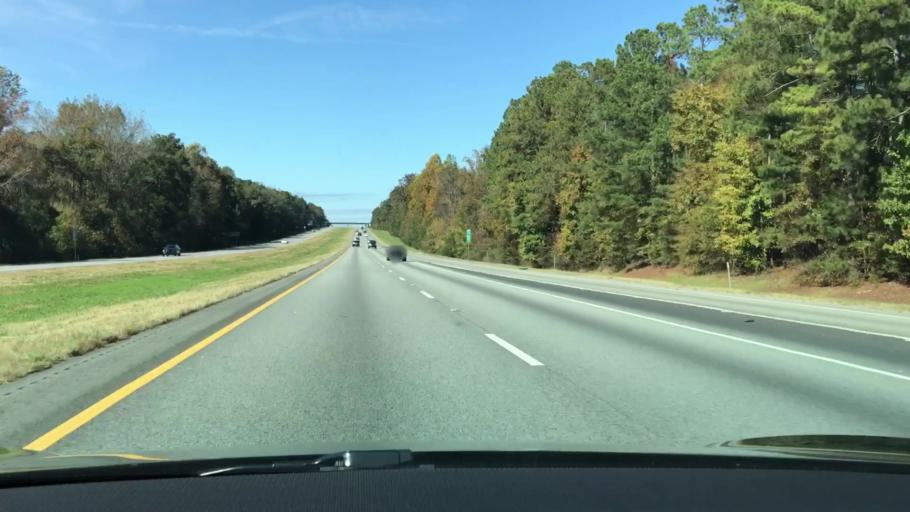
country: US
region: Georgia
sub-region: Morgan County
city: Madison
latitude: 33.5638
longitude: -83.5044
